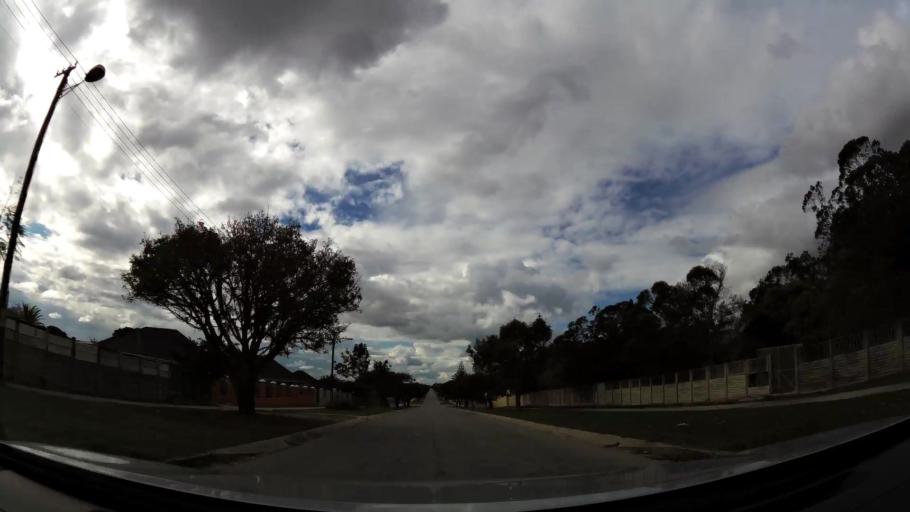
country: ZA
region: Eastern Cape
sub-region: Nelson Mandela Bay Metropolitan Municipality
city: Port Elizabeth
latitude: -33.9416
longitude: 25.5195
